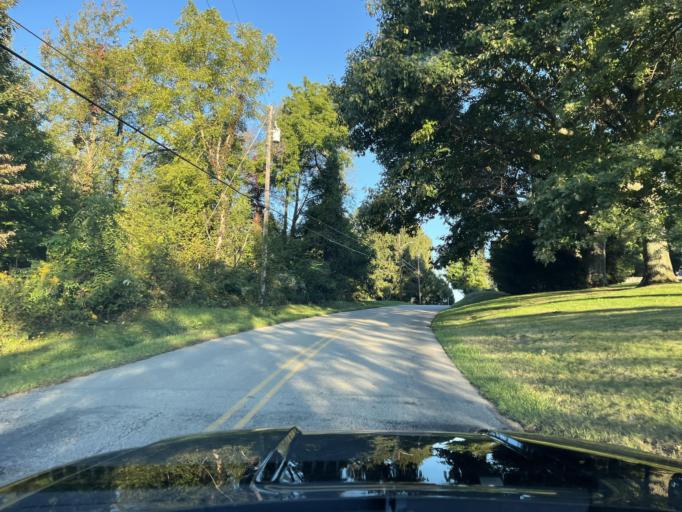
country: US
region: Pennsylvania
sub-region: Fayette County
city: Leith-Hatfield
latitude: 39.8688
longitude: -79.7371
